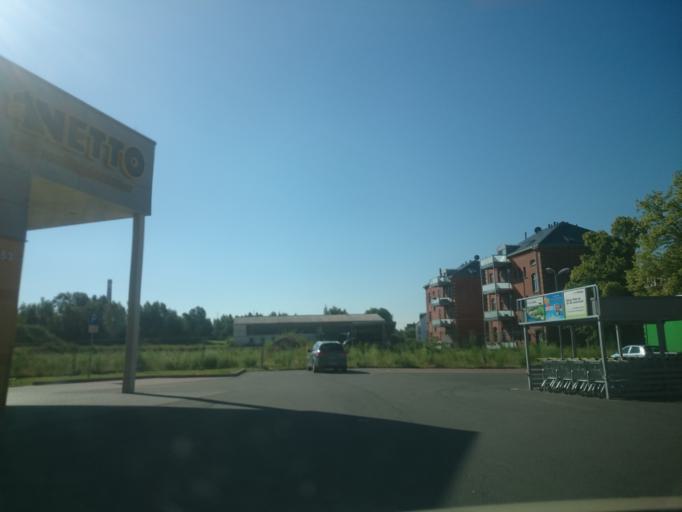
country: DE
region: Saxony
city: Freiberg
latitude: 50.9118
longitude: 13.3576
